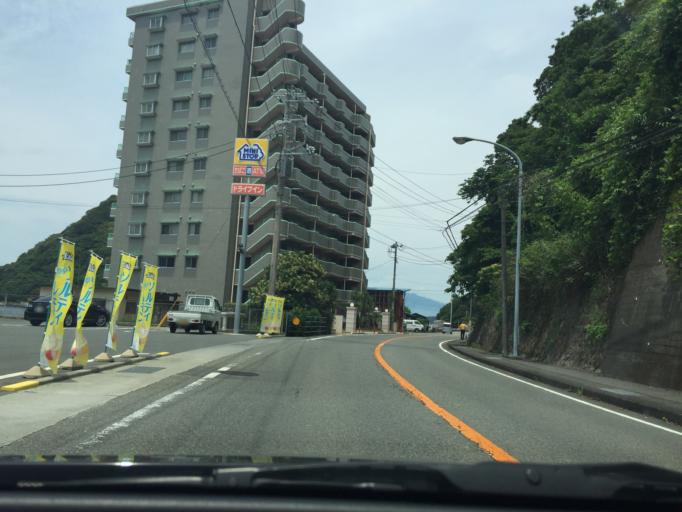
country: JP
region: Shizuoka
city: Numazu
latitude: 35.0280
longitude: 138.8937
